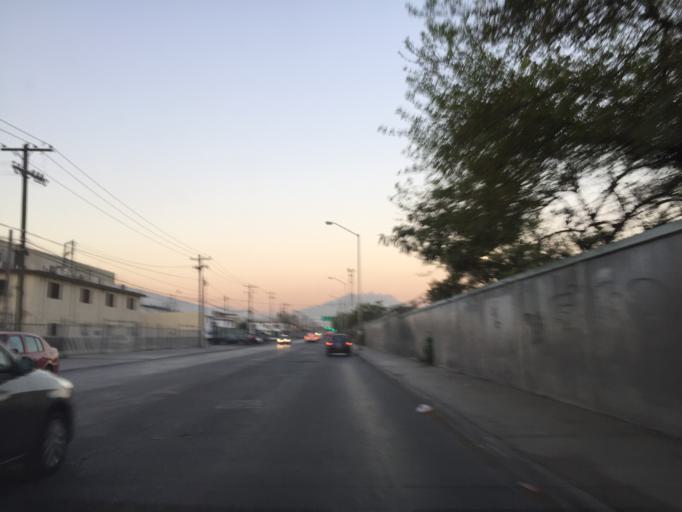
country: MX
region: Nuevo Leon
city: Guadalupe
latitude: 25.6953
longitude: -100.2249
